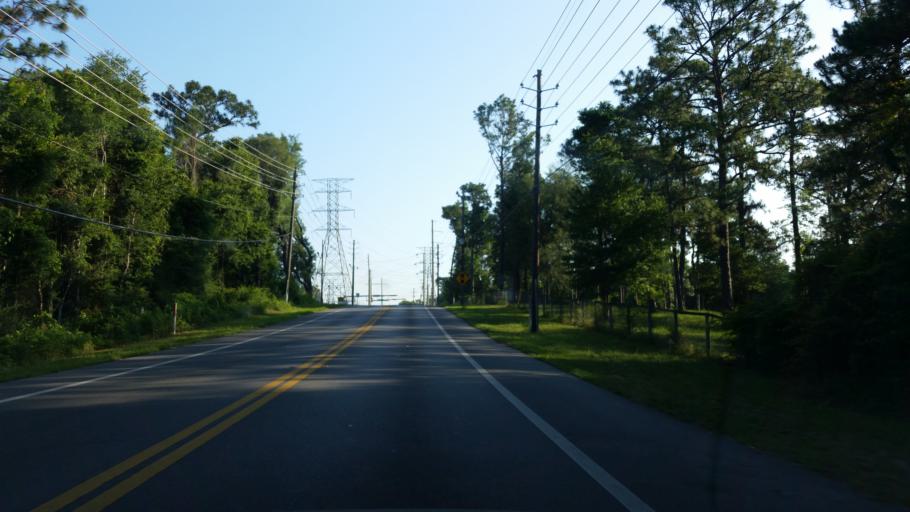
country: US
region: Florida
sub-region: Escambia County
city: Ferry Pass
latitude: 30.5304
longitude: -87.2373
